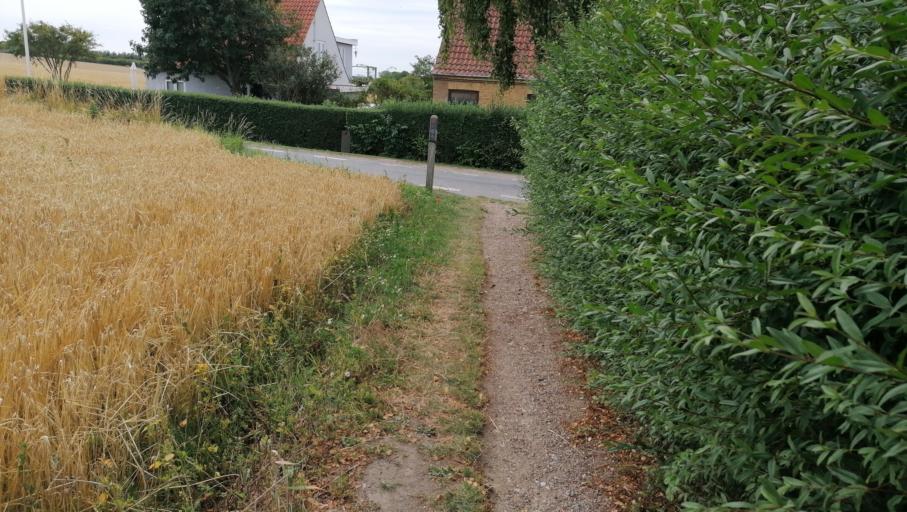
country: DK
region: Zealand
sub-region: Odsherred Kommune
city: Horve
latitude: 55.7511
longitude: 11.4180
